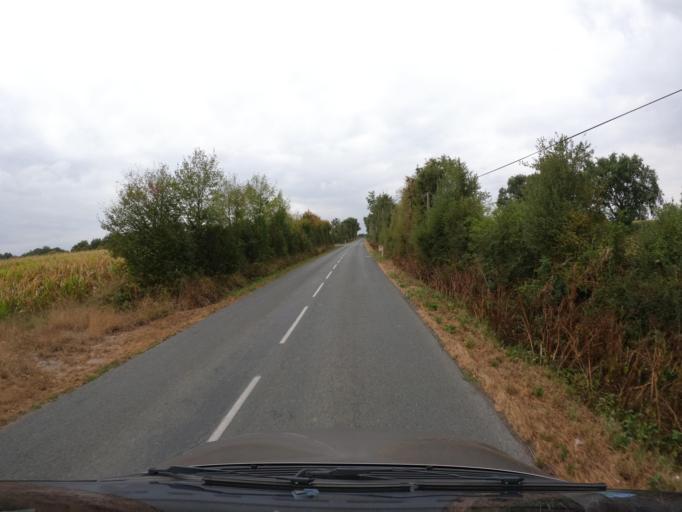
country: FR
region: Pays de la Loire
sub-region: Departement de la Vendee
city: Tiffauges
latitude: 46.9968
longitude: -1.0923
